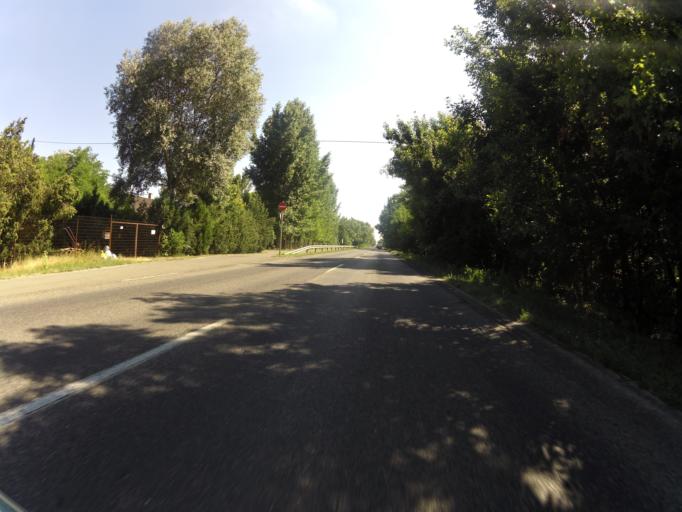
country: HU
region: Csongrad
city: Szatymaz
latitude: 46.3313
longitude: 20.0645
